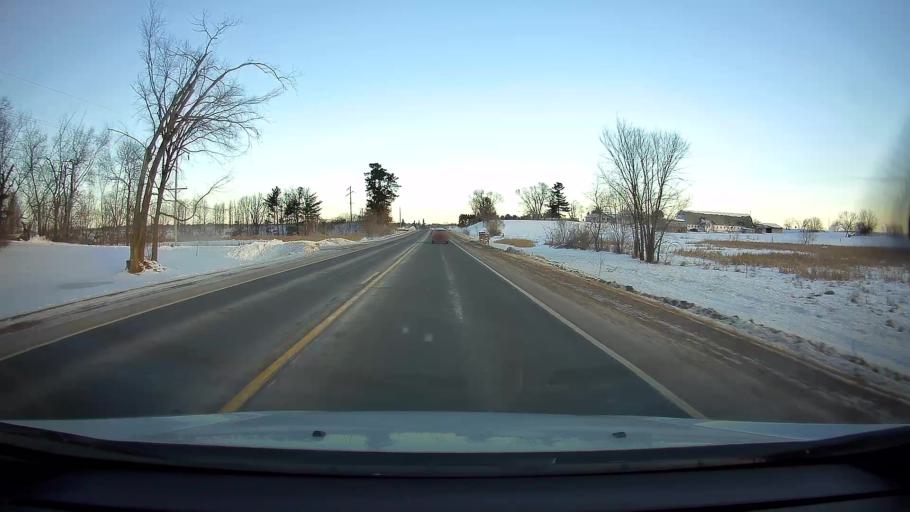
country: US
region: Wisconsin
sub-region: Barron County
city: Turtle Lake
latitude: 45.3778
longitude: -92.1667
